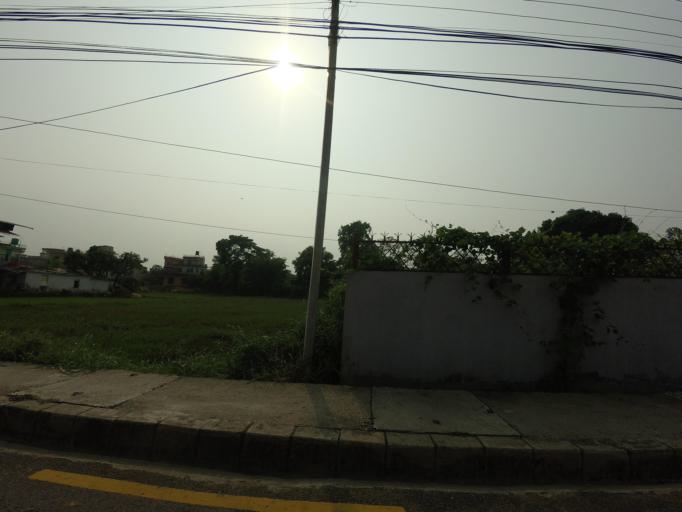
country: NP
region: Western Region
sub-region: Lumbini Zone
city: Bhairahawa
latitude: 27.5238
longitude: 83.4579
